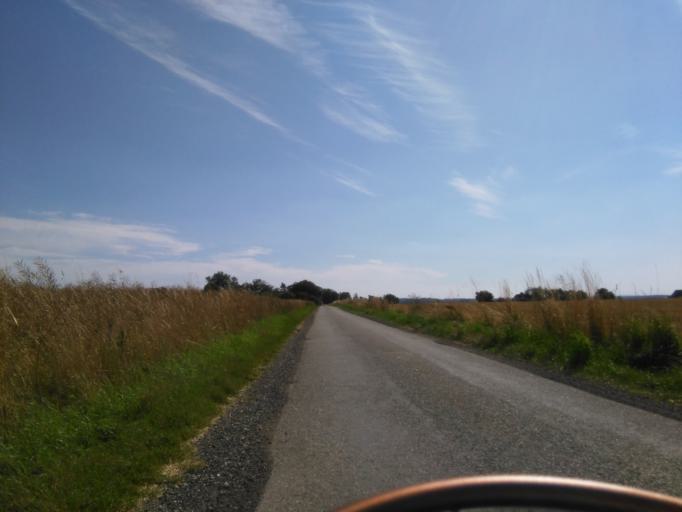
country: DK
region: Central Jutland
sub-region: Hedensted Kommune
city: Juelsminde
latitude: 55.8518
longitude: 10.0476
